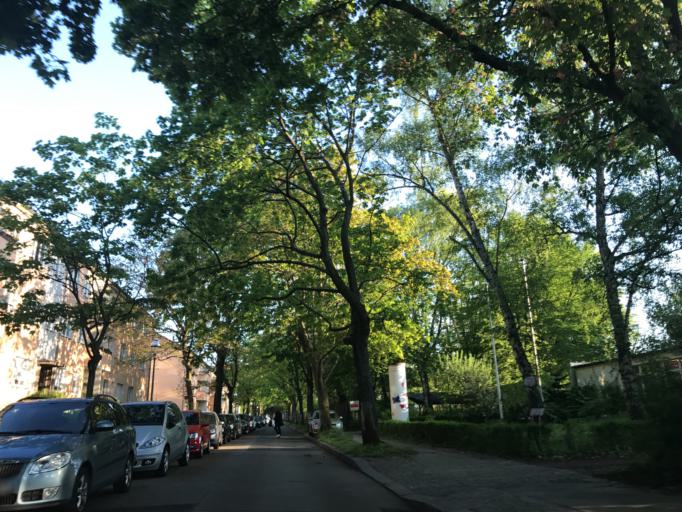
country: DE
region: Berlin
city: Schmargendorf
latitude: 52.4827
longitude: 13.2842
